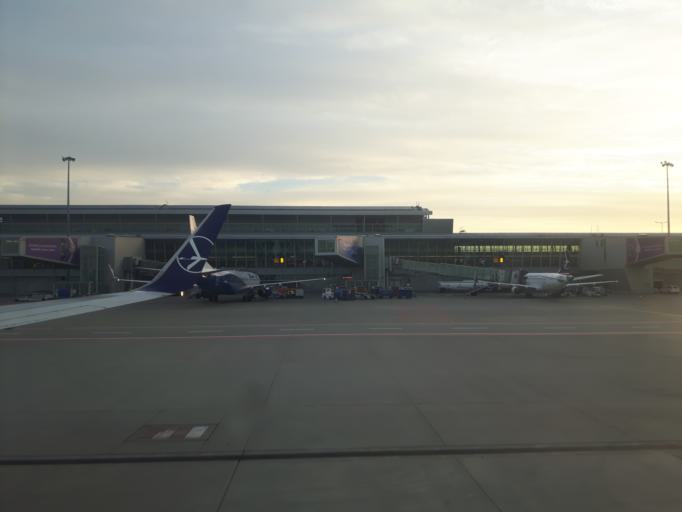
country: PL
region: Masovian Voivodeship
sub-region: Warszawa
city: Wlochy
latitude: 52.1693
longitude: 20.9707
